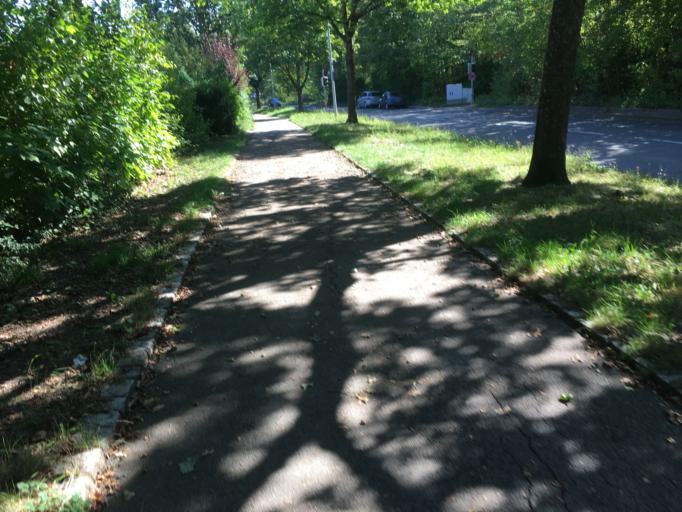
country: DE
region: Baden-Wuerttemberg
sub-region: Regierungsbezirk Stuttgart
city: Boeblingen
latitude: 48.6684
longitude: 8.9939
